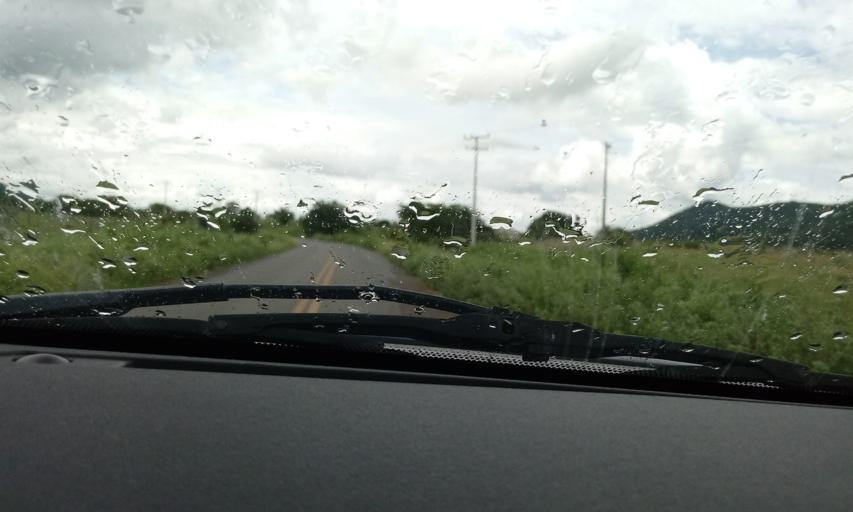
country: BR
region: Bahia
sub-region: Guanambi
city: Guanambi
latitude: -14.0944
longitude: -42.8724
